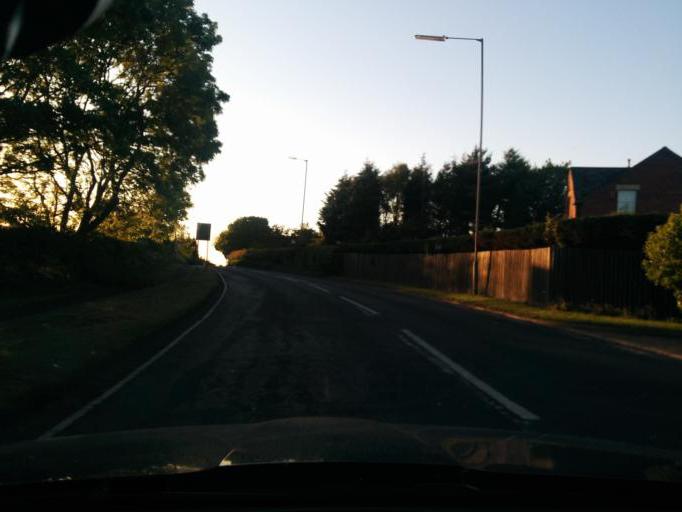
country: GB
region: England
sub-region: Northumberland
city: Bedlington
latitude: 55.1397
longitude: -1.5983
